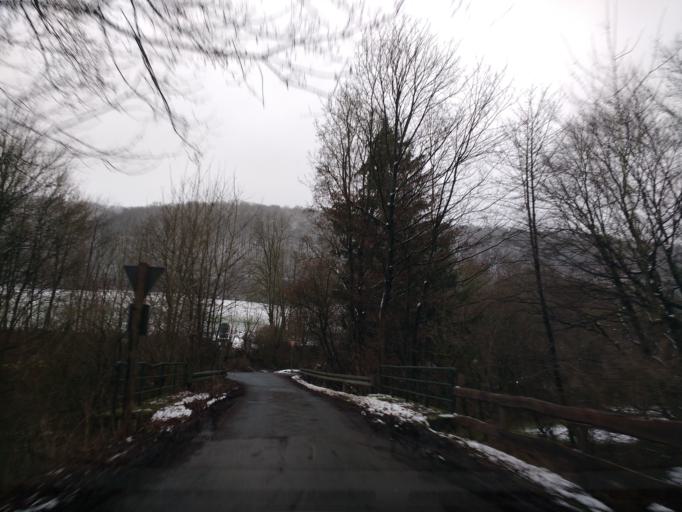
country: DE
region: North Rhine-Westphalia
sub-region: Regierungsbezirk Detmold
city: Altenbeken
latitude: 51.7582
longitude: 8.9059
